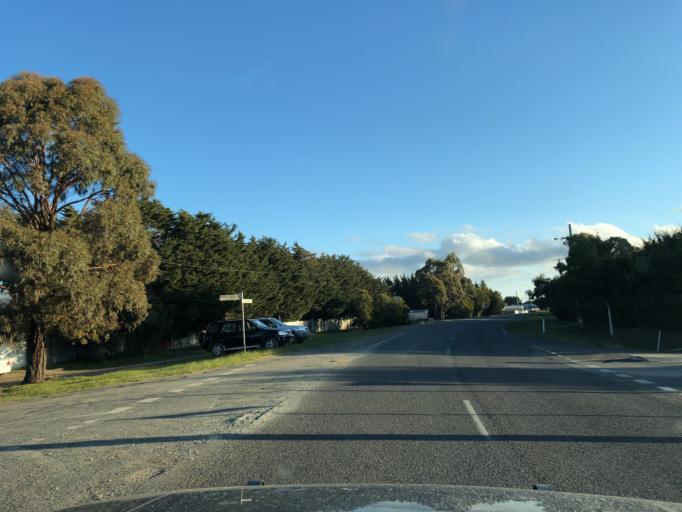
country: AU
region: Victoria
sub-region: Moorabool
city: Bacchus Marsh
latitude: -37.5924
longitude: 144.2353
